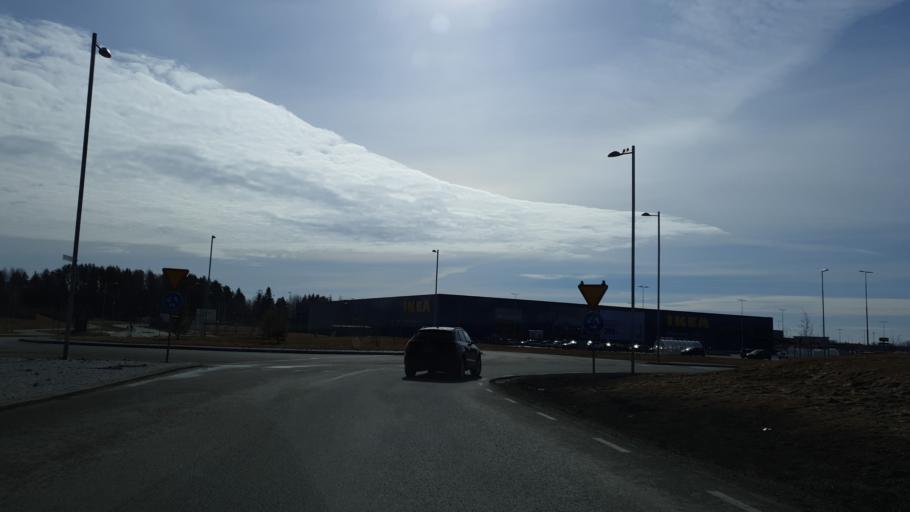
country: SE
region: Vaesterbotten
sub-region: Umea Kommun
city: Umea
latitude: 63.8104
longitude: 20.2515
